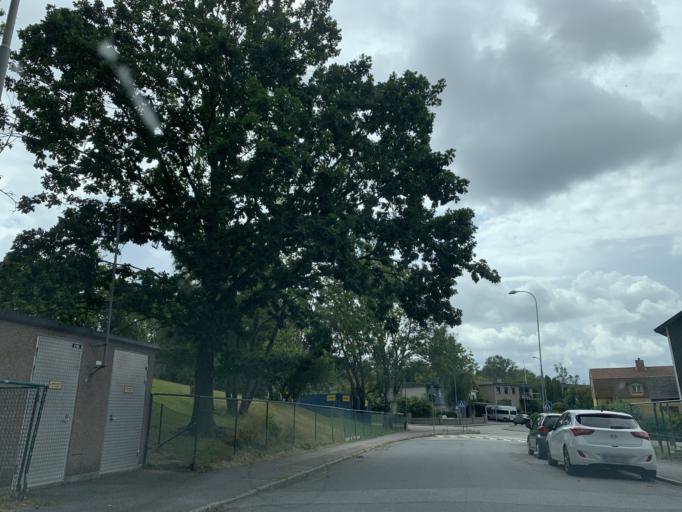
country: SE
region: Vaestra Goetaland
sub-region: Goteborg
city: Eriksbo
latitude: 57.7393
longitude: 12.0488
